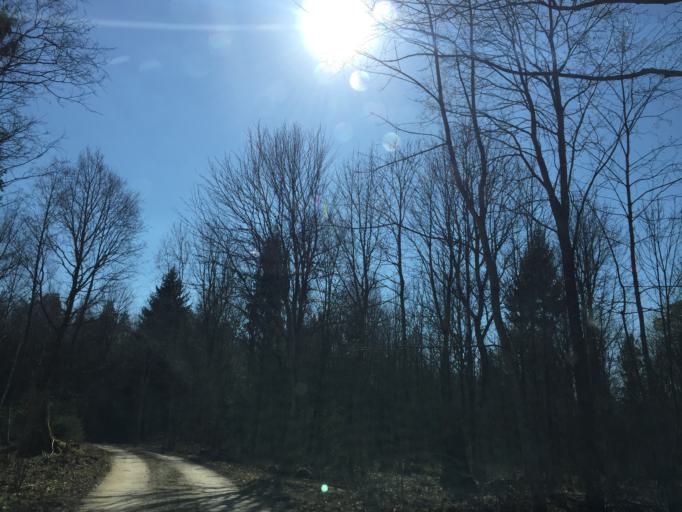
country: EE
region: Viljandimaa
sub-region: Viljandi linn
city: Viljandi
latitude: 58.2732
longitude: 25.6048
